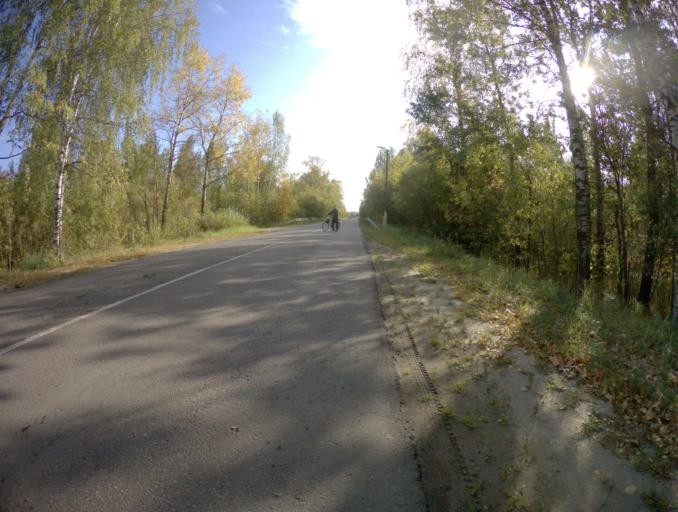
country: RU
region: Moskovskaya
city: Roshal'
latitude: 55.6580
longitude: 39.8344
